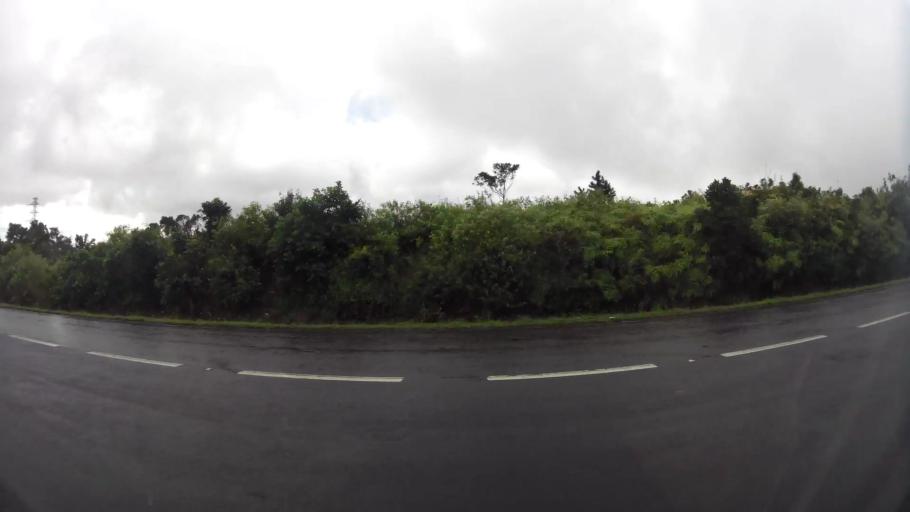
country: MU
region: Plaines Wilhems
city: Curepipe
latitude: -20.3006
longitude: 57.5363
